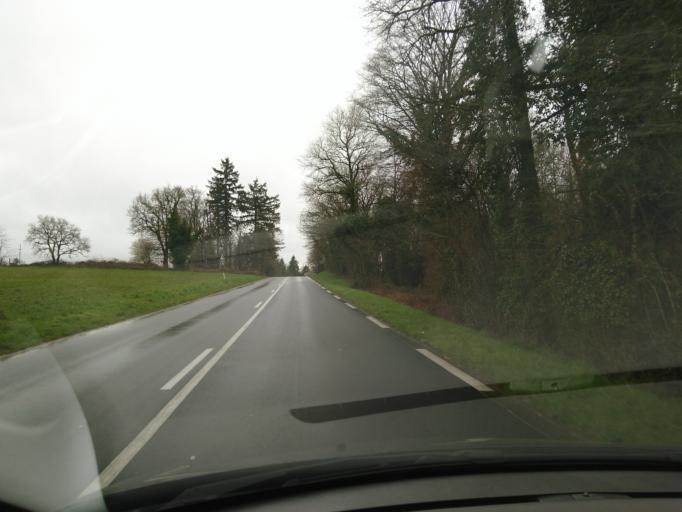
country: FR
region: Limousin
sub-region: Departement de la Haute-Vienne
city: Condat-sur-Vienne
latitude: 45.7739
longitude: 1.2893
